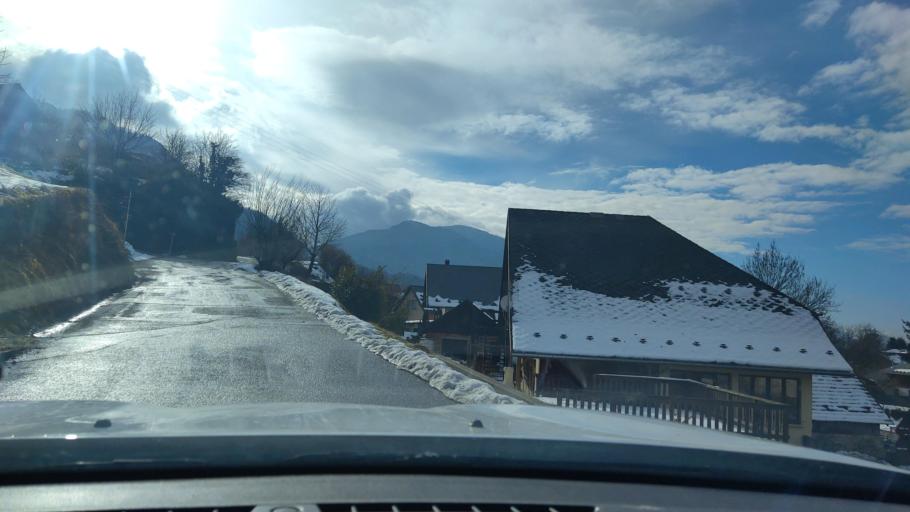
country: FR
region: Rhone-Alpes
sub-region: Departement de la Savoie
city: Marthod
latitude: 45.6979
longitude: 6.4121
